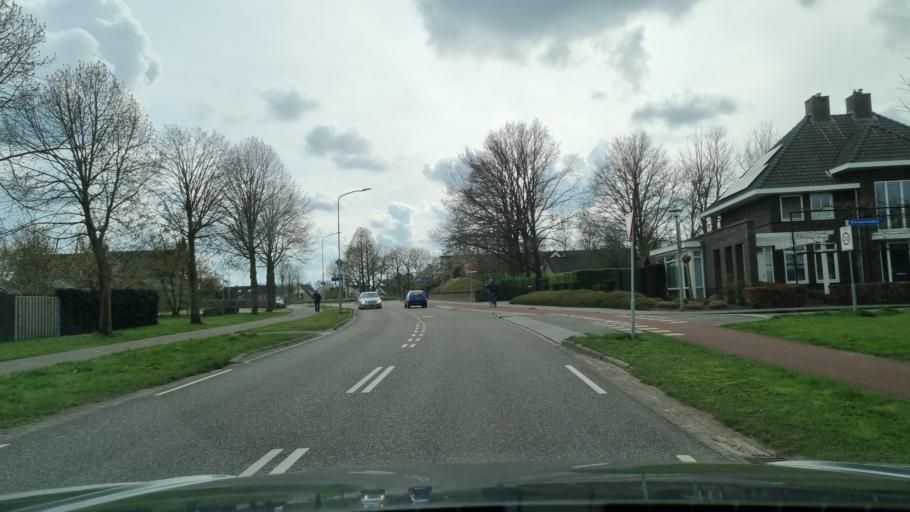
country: NL
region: Gelderland
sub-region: Gemeente Groesbeek
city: Groesbeek
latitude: 51.7744
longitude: 5.9478
